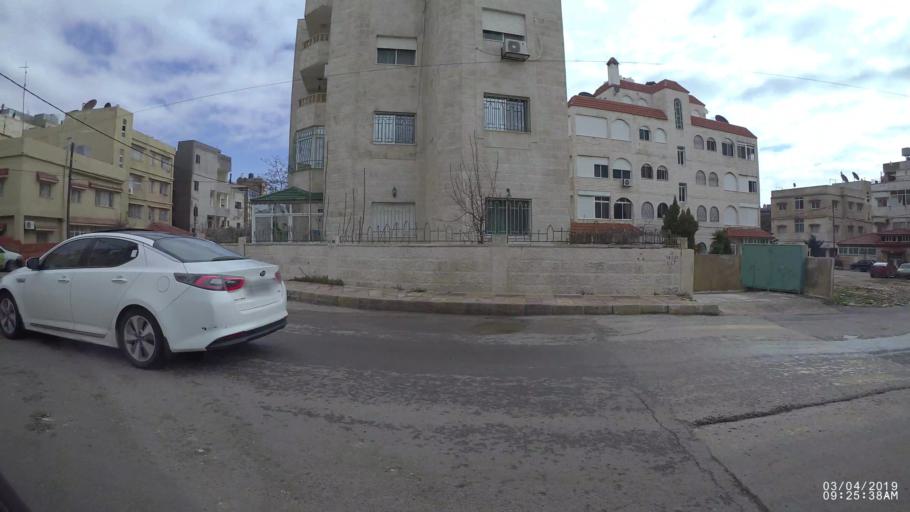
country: JO
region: Amman
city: Wadi as Sir
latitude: 31.9482
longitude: 35.8360
